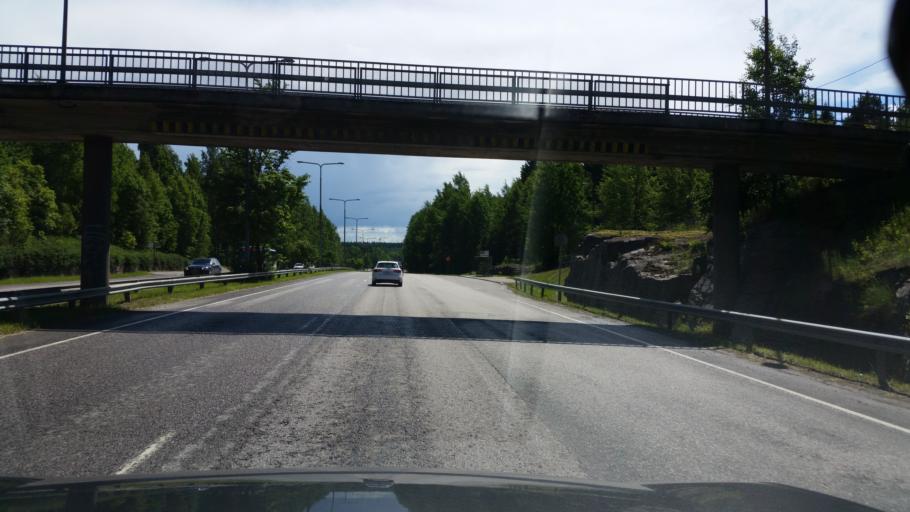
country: FI
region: Uusimaa
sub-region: Helsinki
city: Helsinki
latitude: 60.2331
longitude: 24.9017
